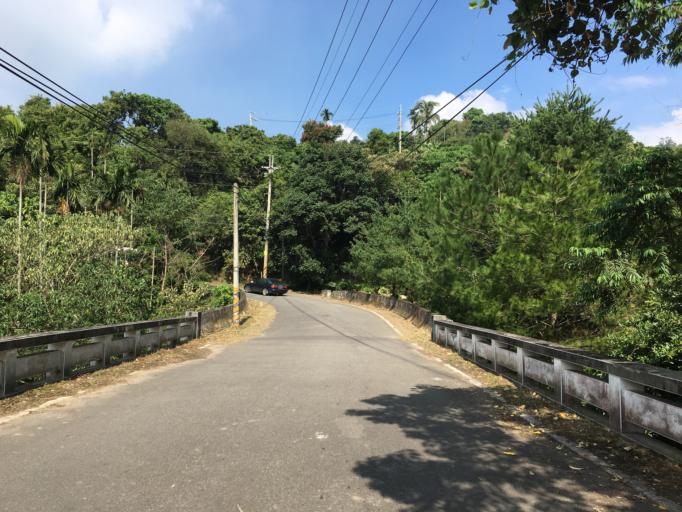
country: TW
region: Taiwan
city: Fengyuan
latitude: 24.1780
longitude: 120.7833
